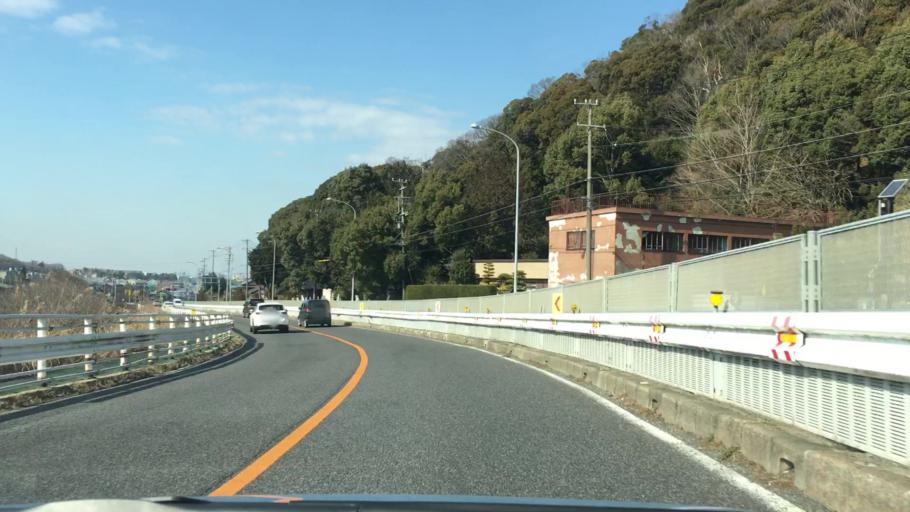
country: JP
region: Aichi
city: Okazaki
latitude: 34.9101
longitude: 137.2288
